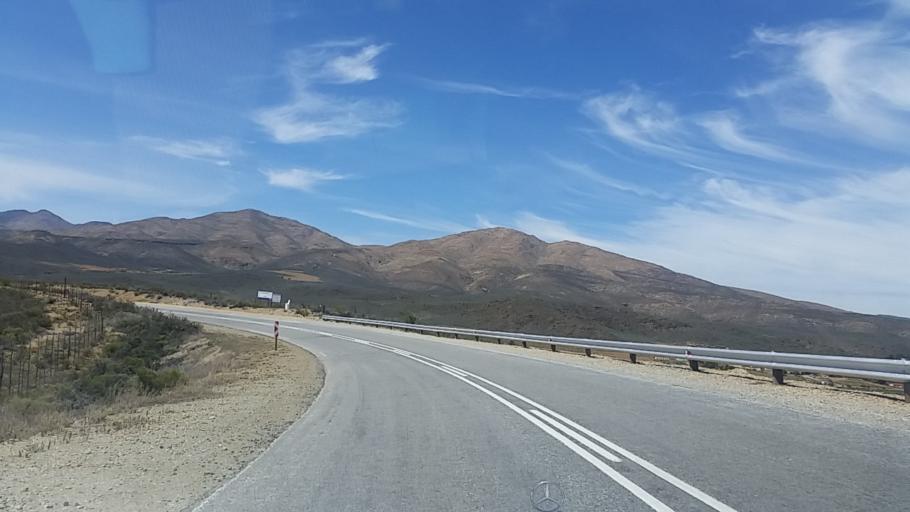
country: ZA
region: Western Cape
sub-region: Eden District Municipality
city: Knysna
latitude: -33.6395
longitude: 23.1302
